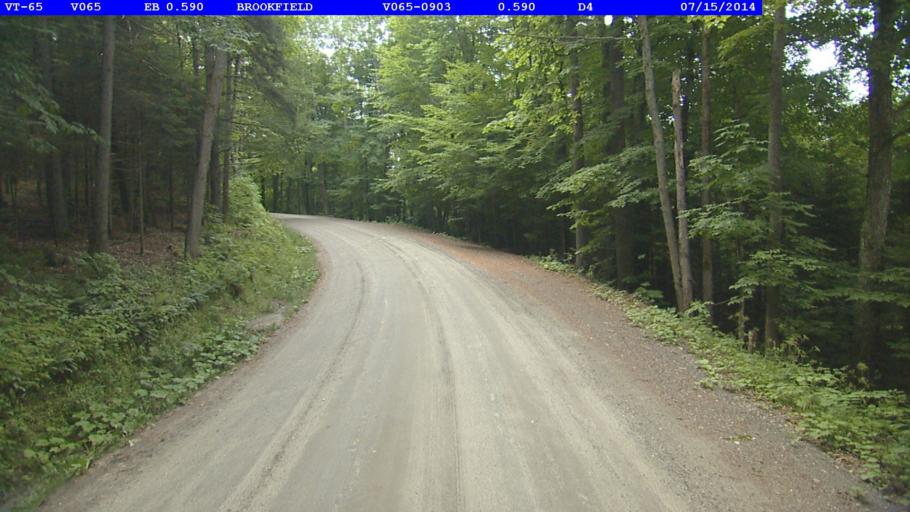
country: US
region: Vermont
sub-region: Washington County
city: Northfield
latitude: 44.0604
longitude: -72.6309
